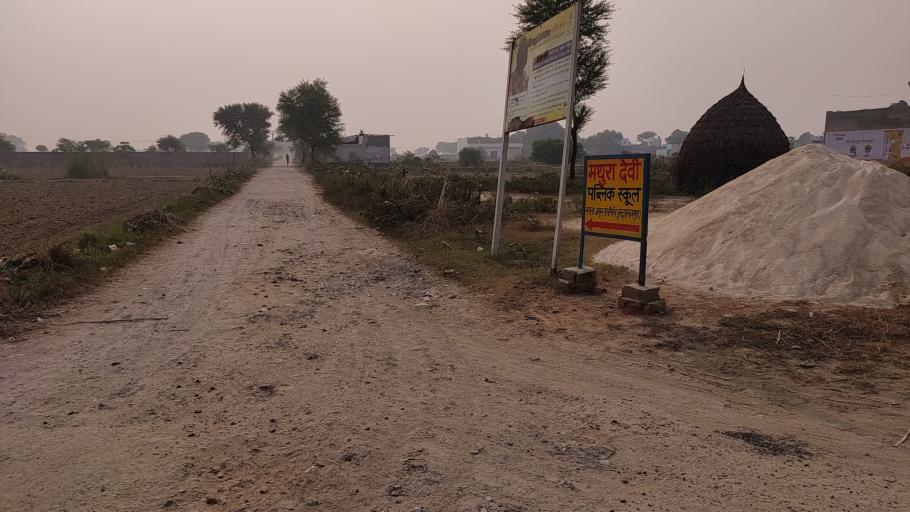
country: IN
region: Uttar Pradesh
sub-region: Mathura
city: Vrindavan
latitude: 27.5563
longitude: 77.7169
